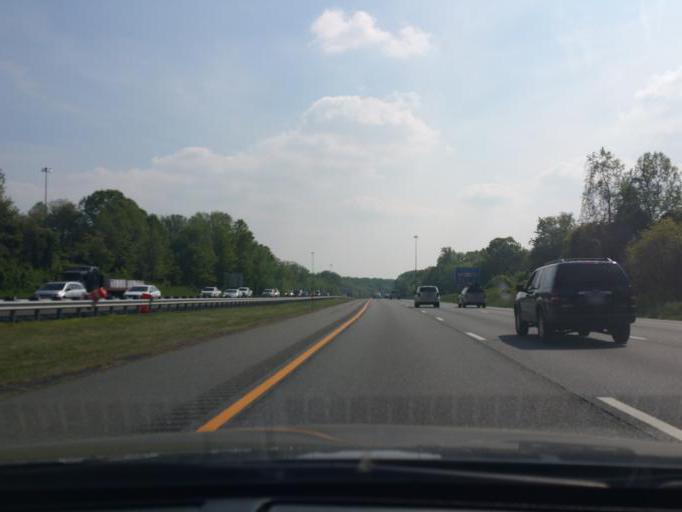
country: US
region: Maryland
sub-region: Harford County
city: Havre de Grace
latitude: 39.5714
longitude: -76.1379
